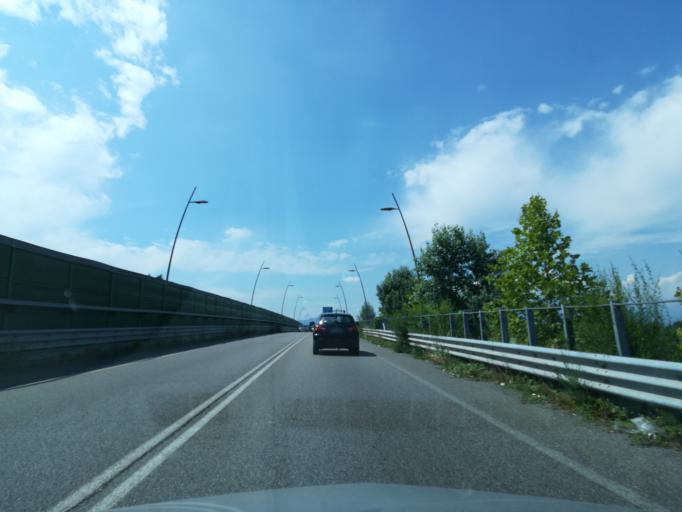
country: IT
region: Lombardy
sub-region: Provincia di Bergamo
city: Stezzano
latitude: 45.6408
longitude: 9.6379
